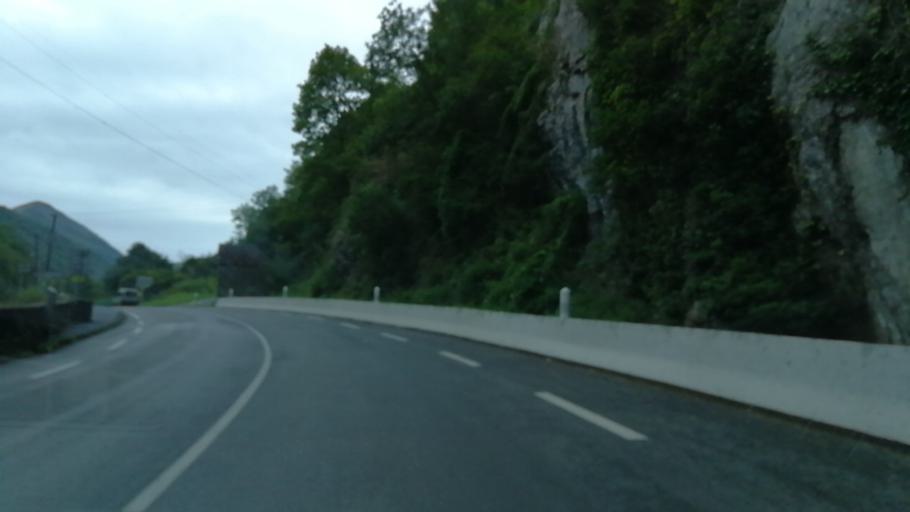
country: FR
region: Aquitaine
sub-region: Departement des Pyrenees-Atlantiques
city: Arette
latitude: 43.0709
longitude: -0.6058
